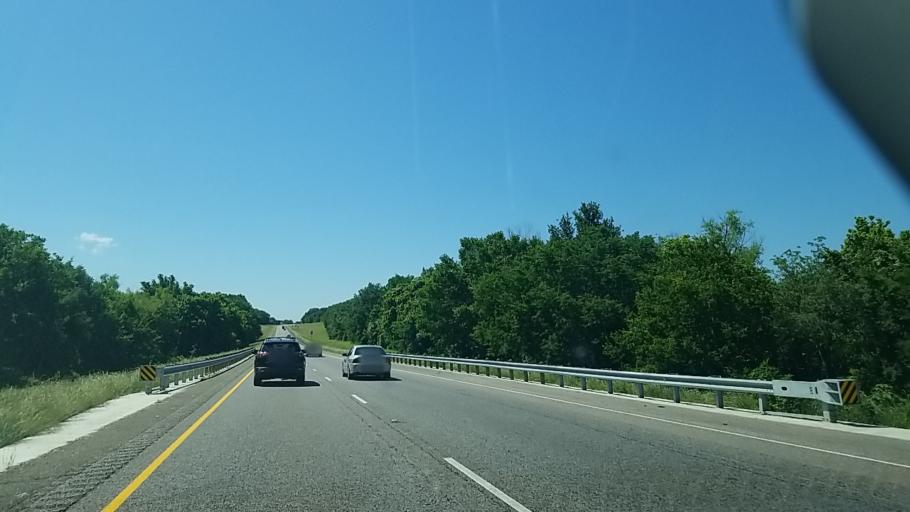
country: US
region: Texas
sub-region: Freestone County
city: Fairfield
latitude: 31.8095
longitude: -96.2677
